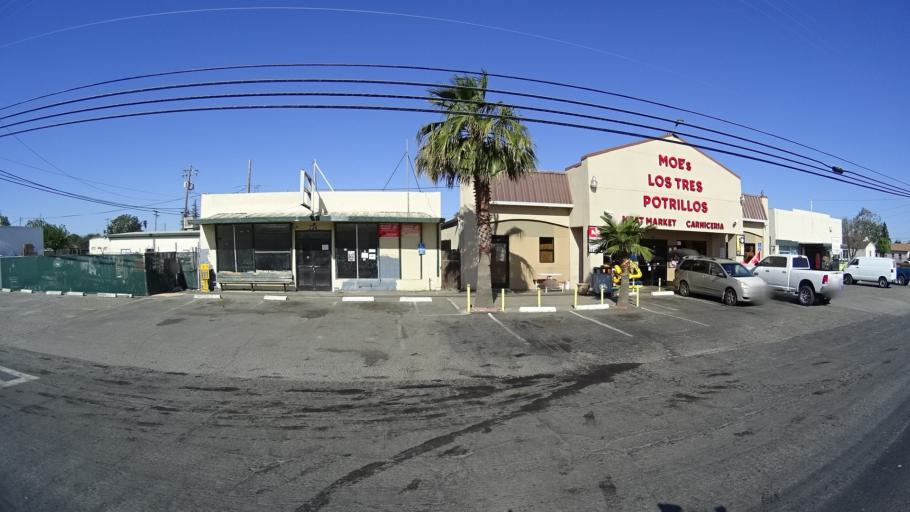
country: US
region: California
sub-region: Glenn County
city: Orland
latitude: 39.7520
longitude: -122.1970
